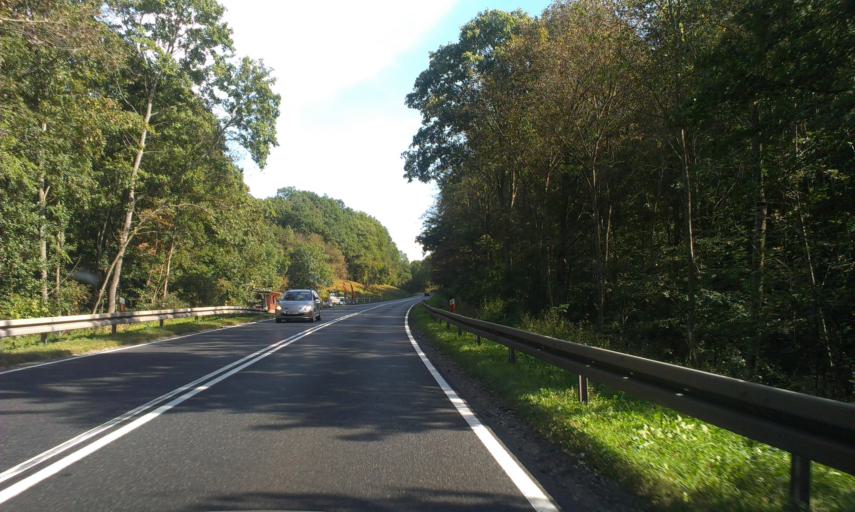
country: PL
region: Greater Poland Voivodeship
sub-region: Powiat pilski
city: Osiek nad Notecia
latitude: 53.1555
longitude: 17.3405
